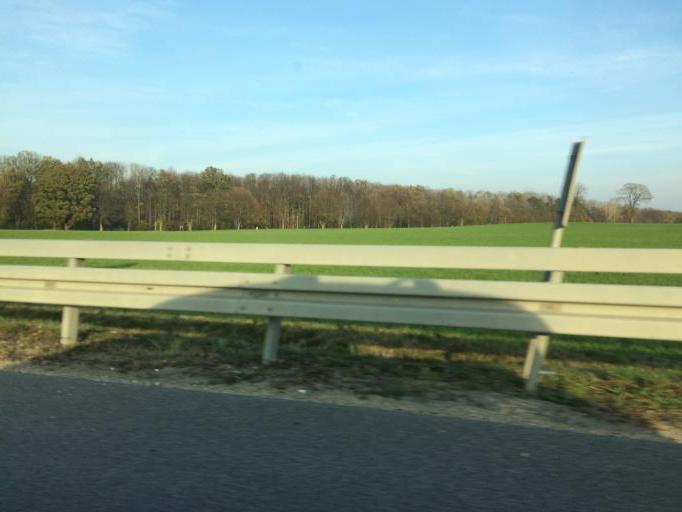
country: PL
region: Opole Voivodeship
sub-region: Powiat strzelecki
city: Strzelce Opolskie
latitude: 50.5003
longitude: 18.3379
